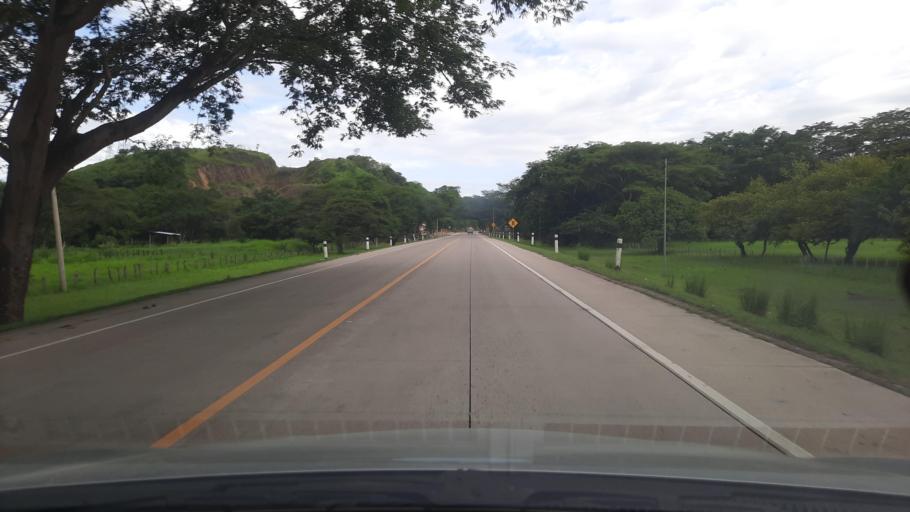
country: NI
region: Chinandega
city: Somotillo
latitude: 12.8697
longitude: -86.8514
